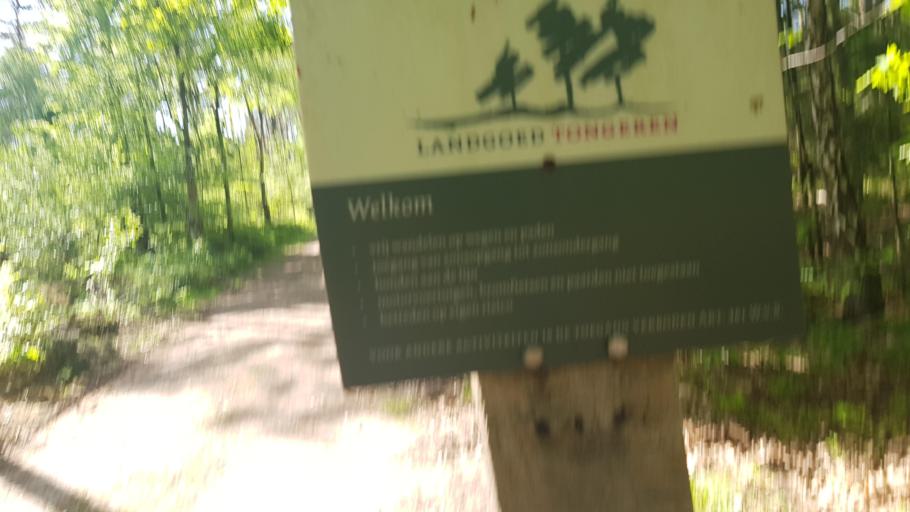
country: NL
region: Gelderland
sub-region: Gemeente Epe
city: Emst
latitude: 52.3449
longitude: 5.9142
